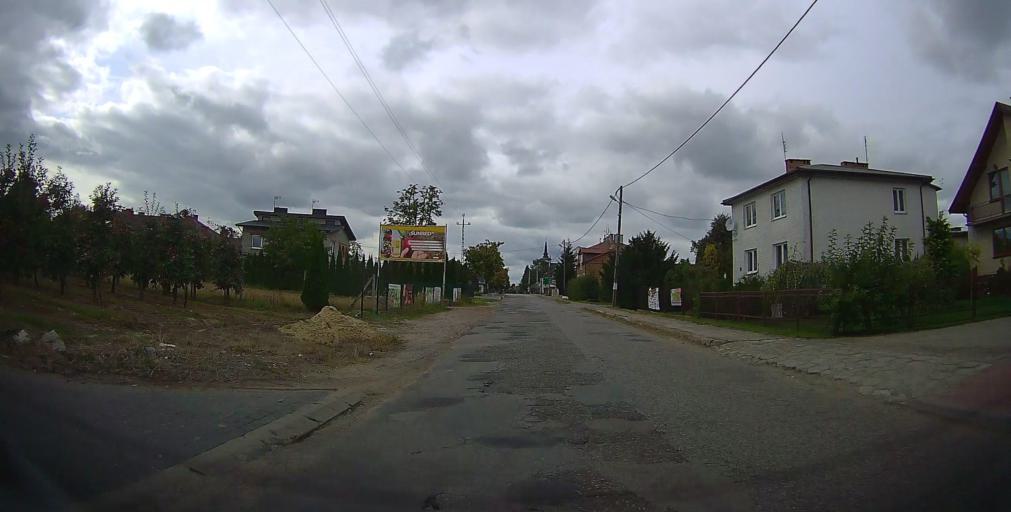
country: PL
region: Masovian Voivodeship
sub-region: Powiat grojecki
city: Belsk Duzy
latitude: 51.8245
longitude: 20.8120
